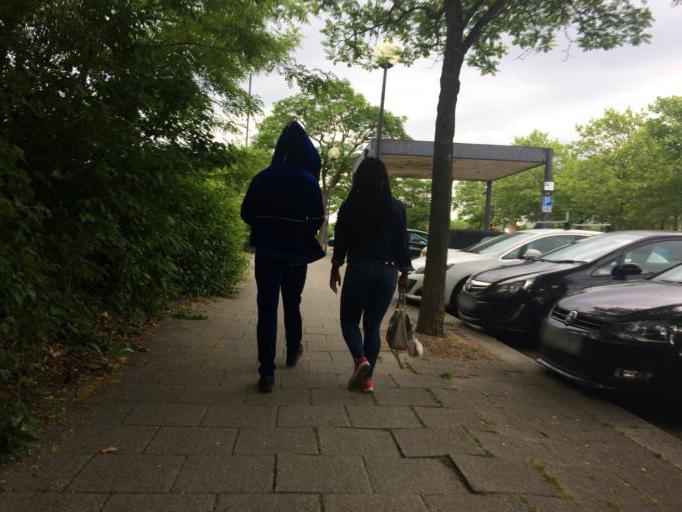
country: GB
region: England
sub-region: Milton Keynes
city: Milton Keynes
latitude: 52.0410
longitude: -0.7538
